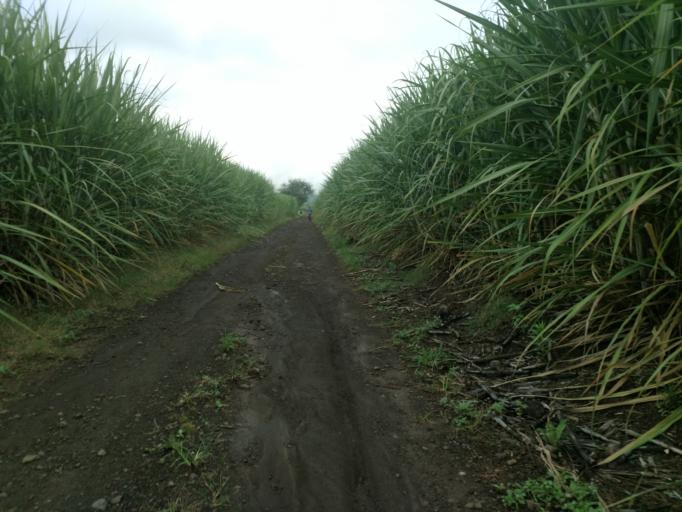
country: MX
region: Nayarit
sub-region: Tepic
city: La Corregidora
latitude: 21.4722
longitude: -104.8040
